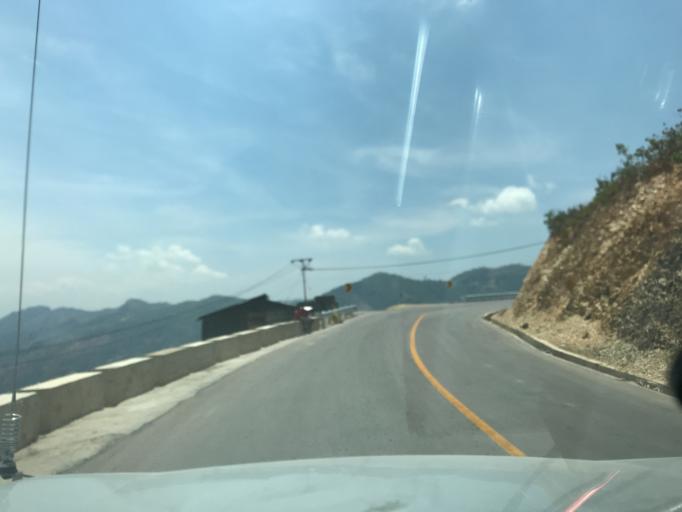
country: TL
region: Aileu
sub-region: Aileu Villa
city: Aileu
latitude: -8.8084
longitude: 125.5974
